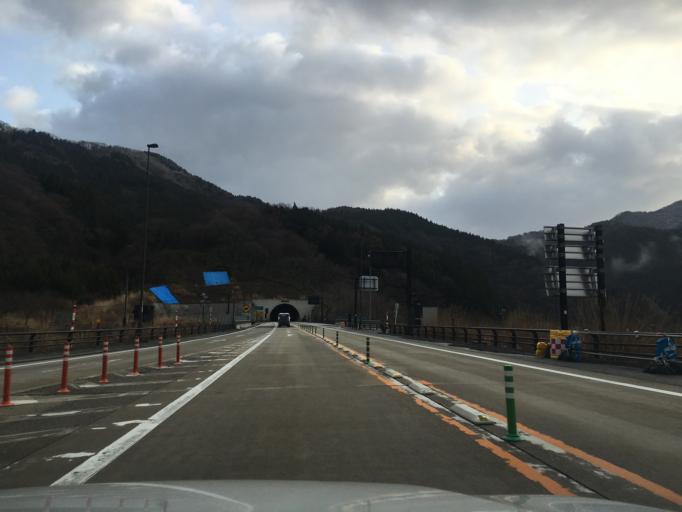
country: JP
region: Yamagata
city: Tsuruoka
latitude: 38.6666
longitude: 139.6239
